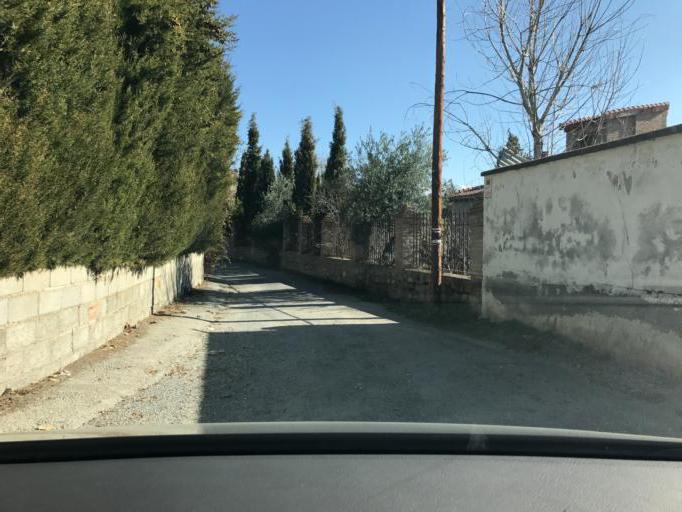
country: ES
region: Andalusia
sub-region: Provincia de Granada
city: Viznar
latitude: 37.2165
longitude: -3.5496
